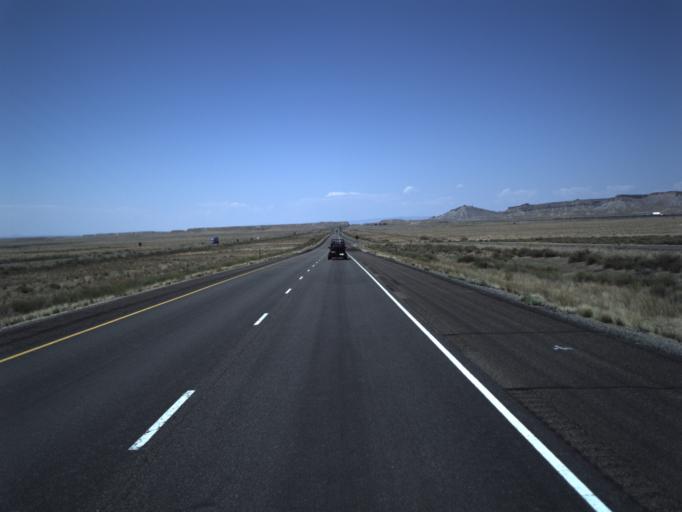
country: US
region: Utah
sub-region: Grand County
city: Moab
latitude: 38.9554
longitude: -109.7539
